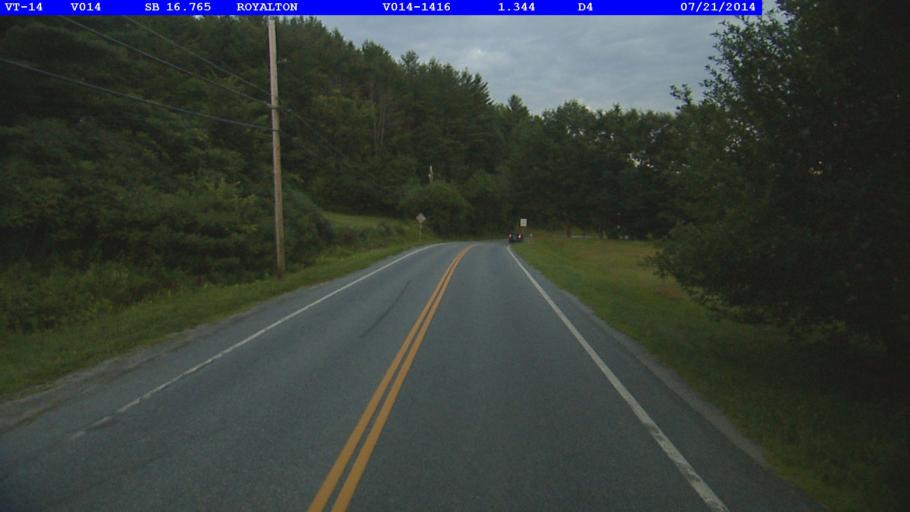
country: US
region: Vermont
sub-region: Orange County
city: Chelsea
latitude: 43.8127
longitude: -72.5062
